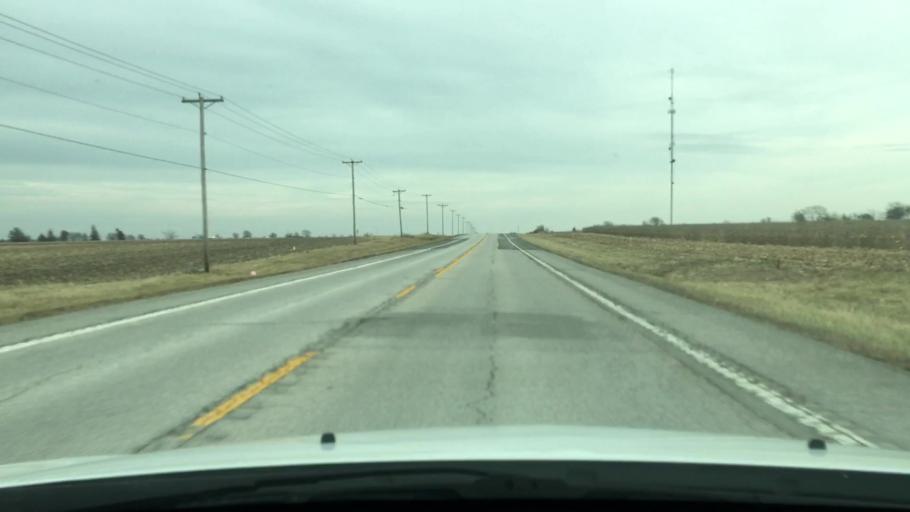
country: US
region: Missouri
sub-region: Pike County
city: Bowling Green
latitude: 39.3448
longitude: -91.3134
